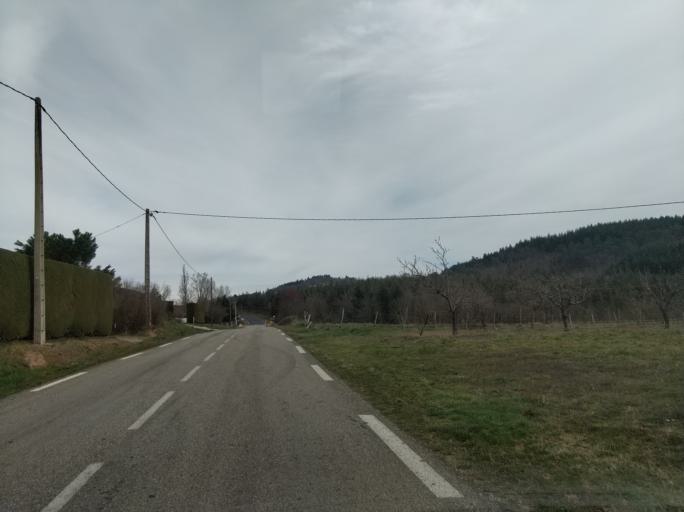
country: FR
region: Rhone-Alpes
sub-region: Departement de l'Ardeche
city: Satillieu
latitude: 45.1696
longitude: 4.6385
